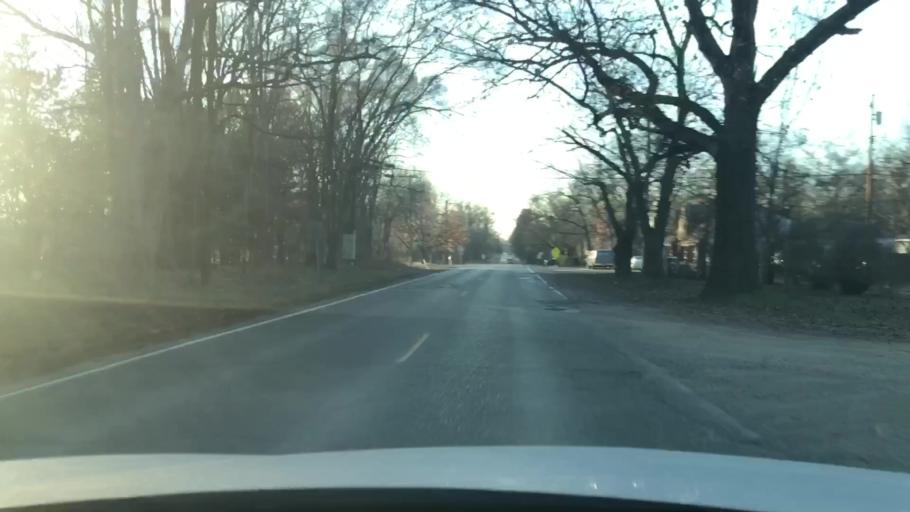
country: US
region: Michigan
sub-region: Oakland County
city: West Bloomfield Township
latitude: 42.5992
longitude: -83.4312
